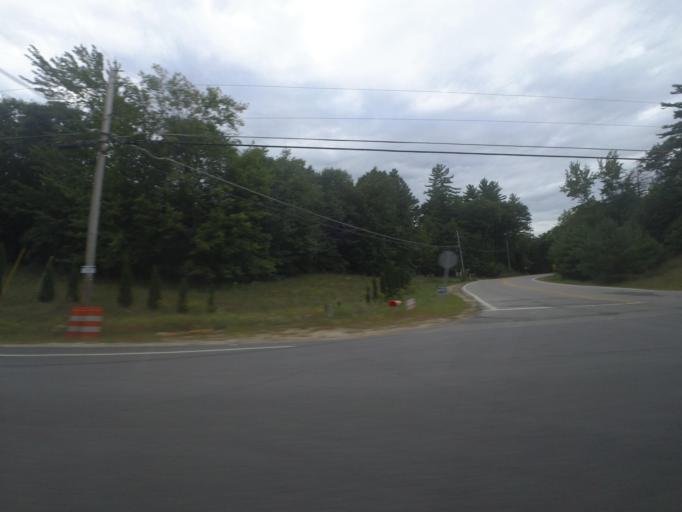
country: US
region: New Hampshire
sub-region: Strafford County
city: Barrington
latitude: 43.2592
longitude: -71.0265
